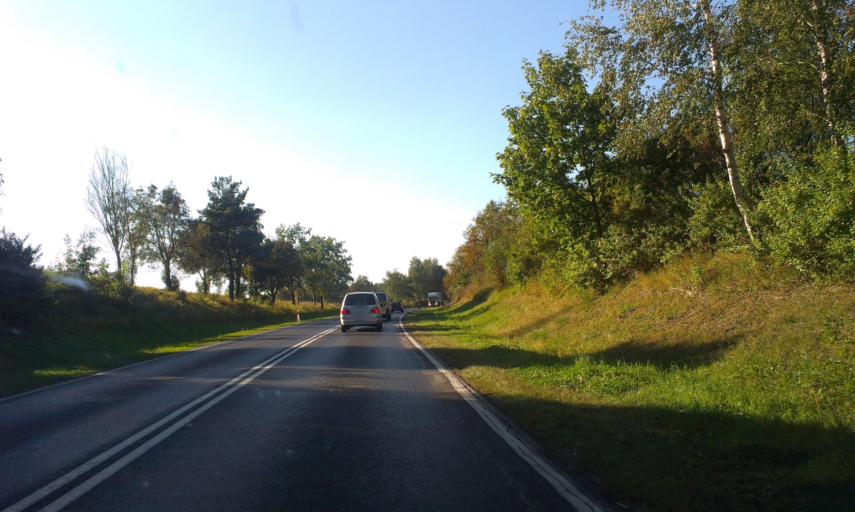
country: PL
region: Kujawsko-Pomorskie
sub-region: Powiat swiecki
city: Swiecie
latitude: 53.4143
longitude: 18.3640
